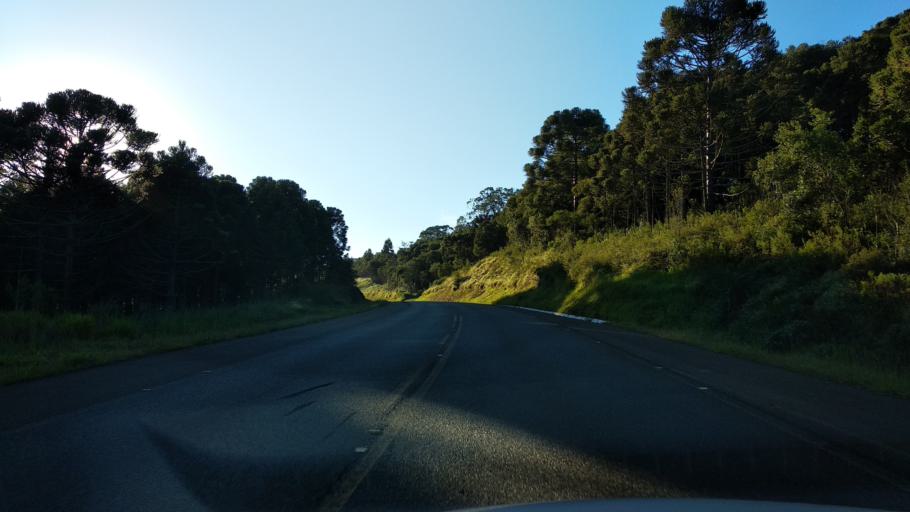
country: BR
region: Santa Catarina
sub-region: Correia Pinto
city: Correia Pinto
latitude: -27.6169
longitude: -50.6827
